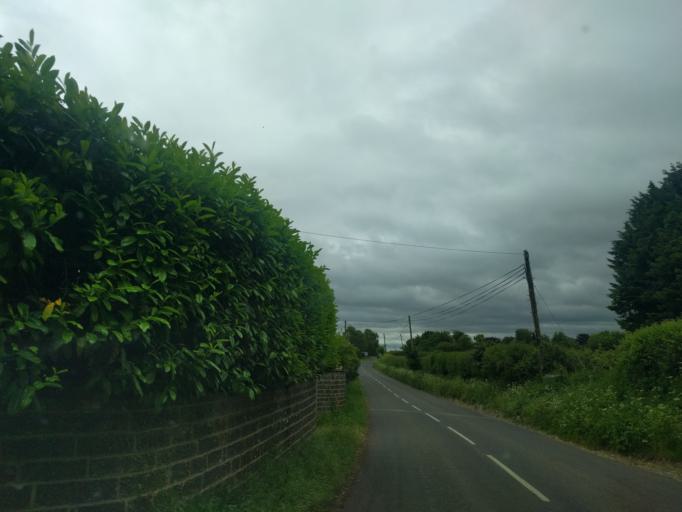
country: GB
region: England
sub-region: Somerset
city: Langport
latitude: 51.0742
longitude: -2.8215
